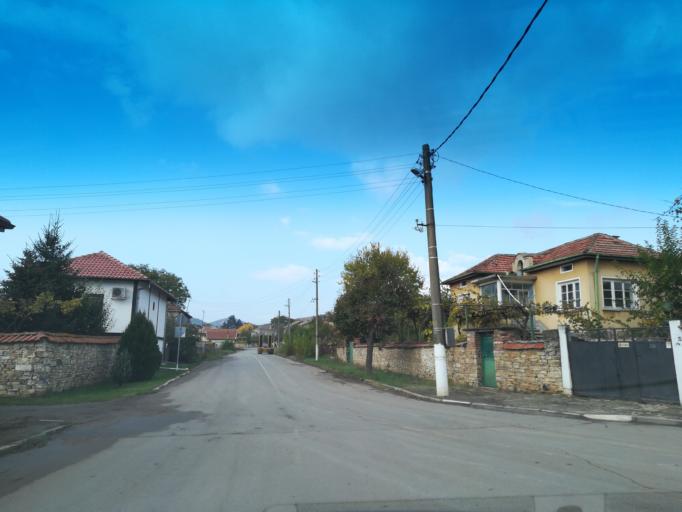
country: BG
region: Stara Zagora
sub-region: Obshtina Nikolaevo
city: Elkhovo
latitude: 42.3404
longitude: 25.4034
